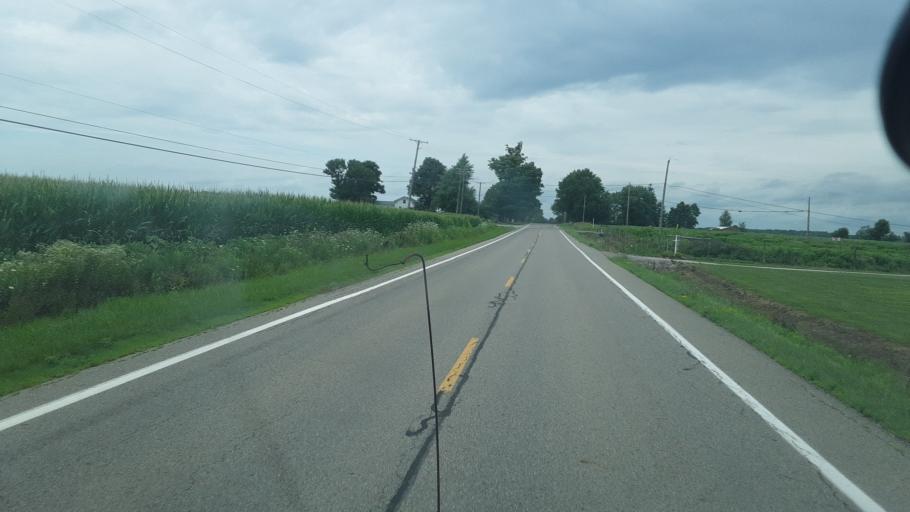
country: US
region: Ohio
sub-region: Trumbull County
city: Cortland
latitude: 41.4113
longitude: -80.6654
